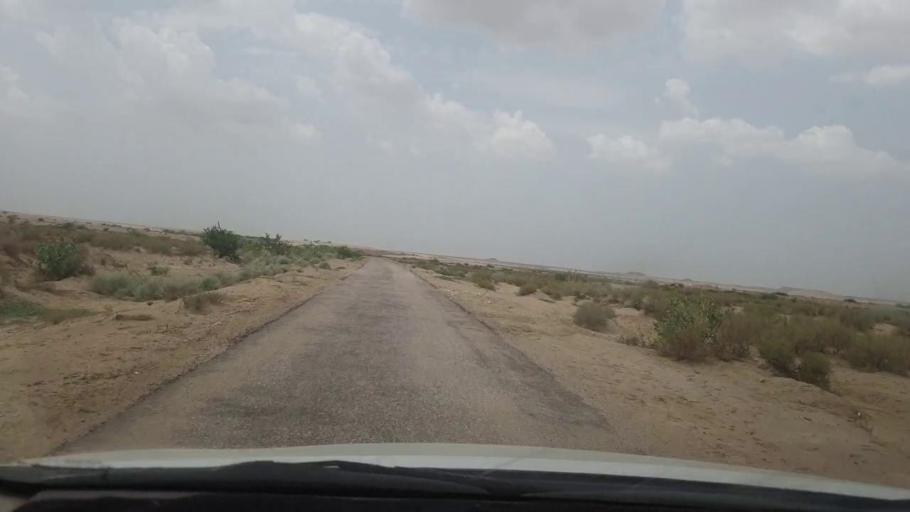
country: PK
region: Sindh
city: Khairpur
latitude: 27.3981
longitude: 68.9753
